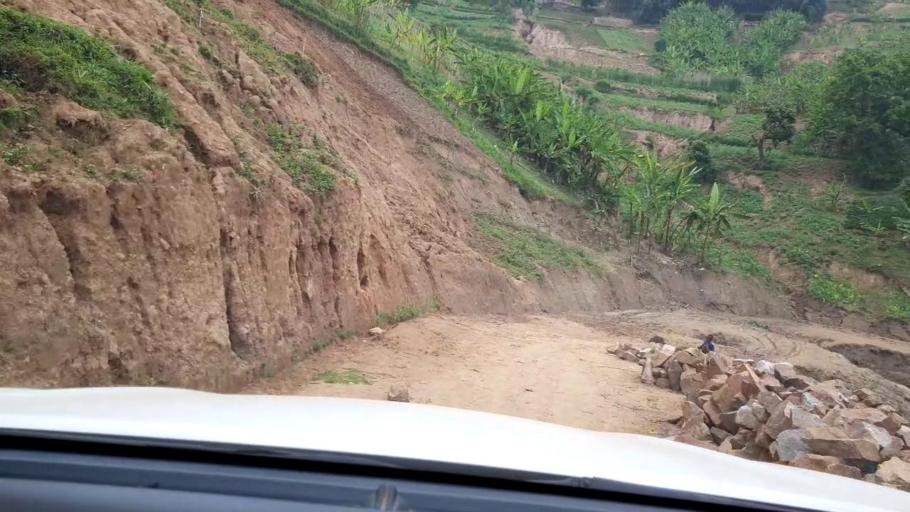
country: RW
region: Western Province
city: Kibuye
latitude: -1.8275
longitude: 29.5454
